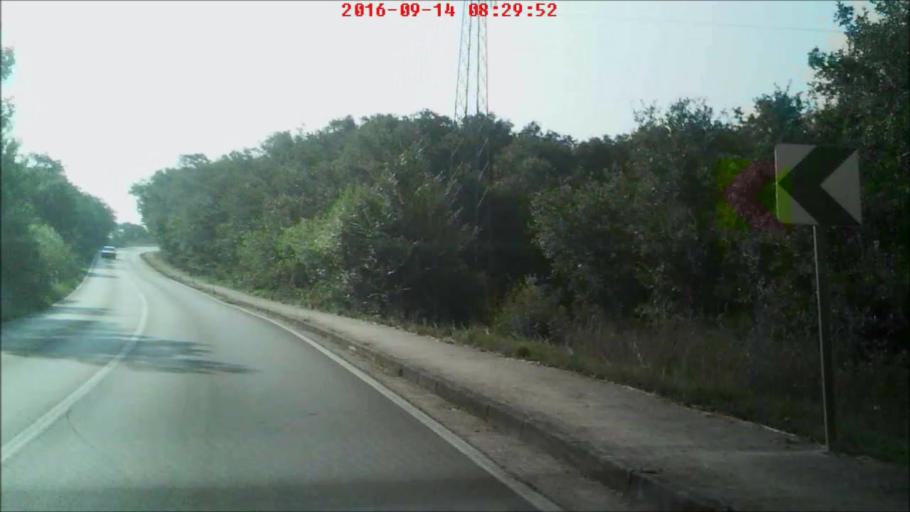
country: HR
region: Zadarska
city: Zadar
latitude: 44.1772
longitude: 15.2871
